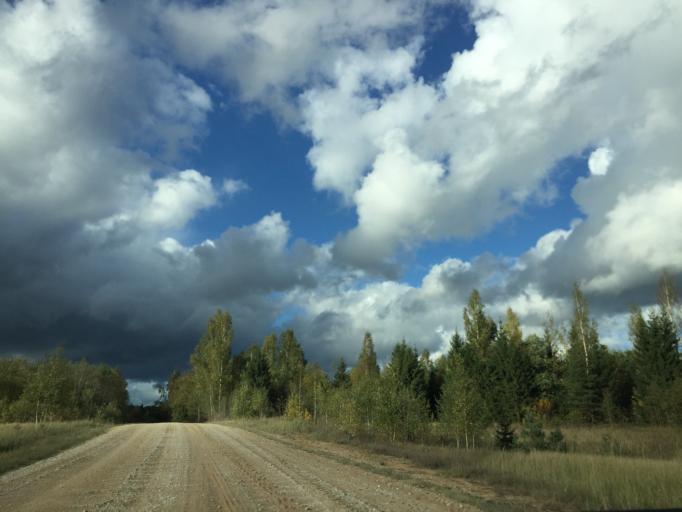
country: LV
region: Malpils
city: Malpils
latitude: 57.0299
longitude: 25.0519
